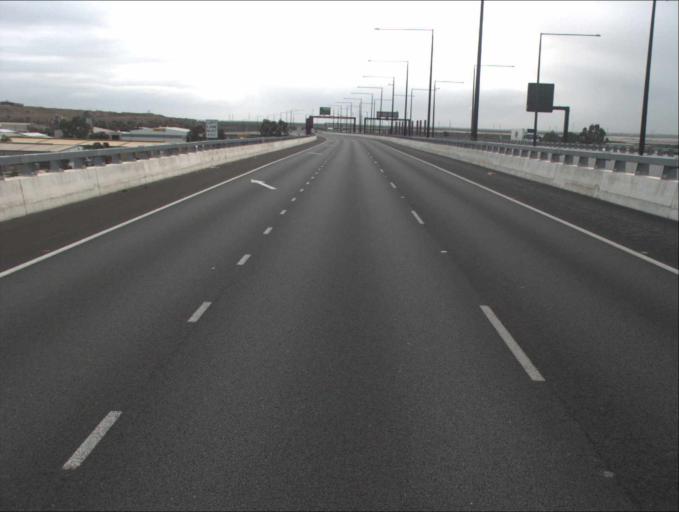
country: AU
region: South Australia
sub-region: Port Adelaide Enfield
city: Blair Athol
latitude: -34.8398
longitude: 138.5636
